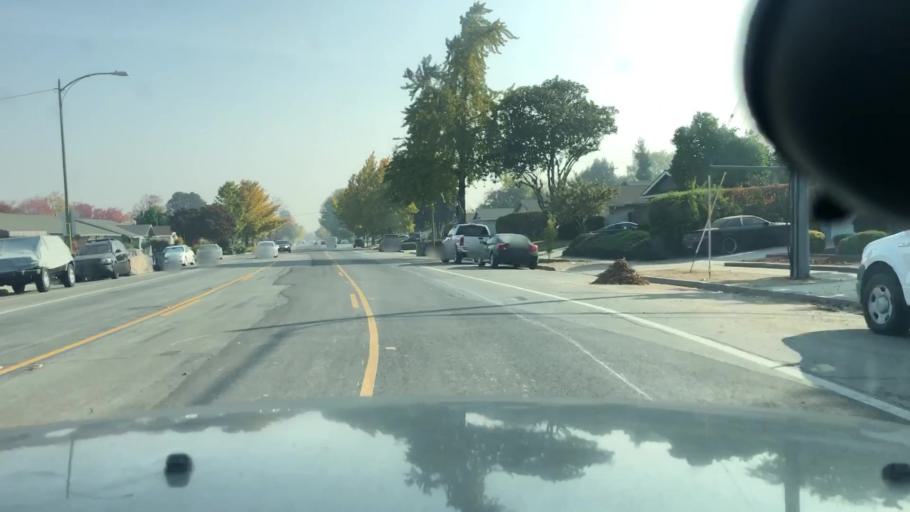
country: US
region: California
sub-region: Santa Clara County
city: Cupertino
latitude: 37.3086
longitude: -121.9926
